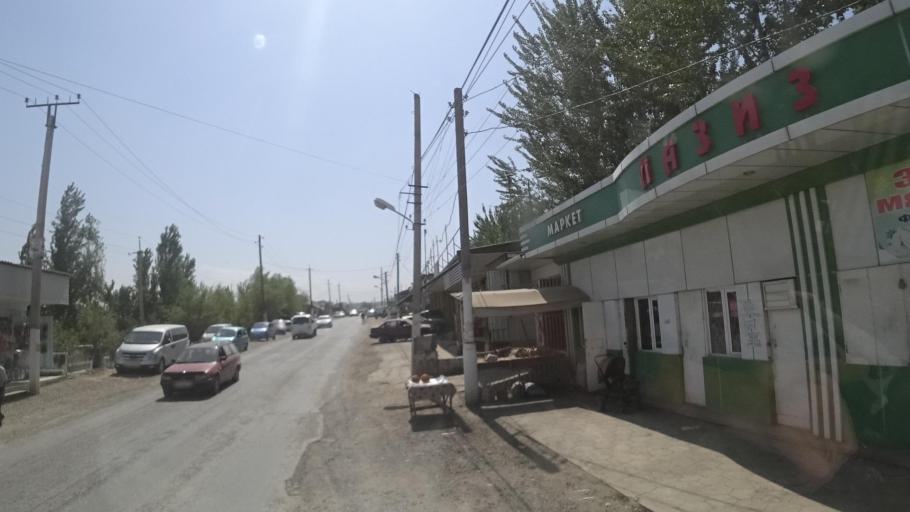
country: KG
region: Osh
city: Osh
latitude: 40.5114
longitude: 72.8299
